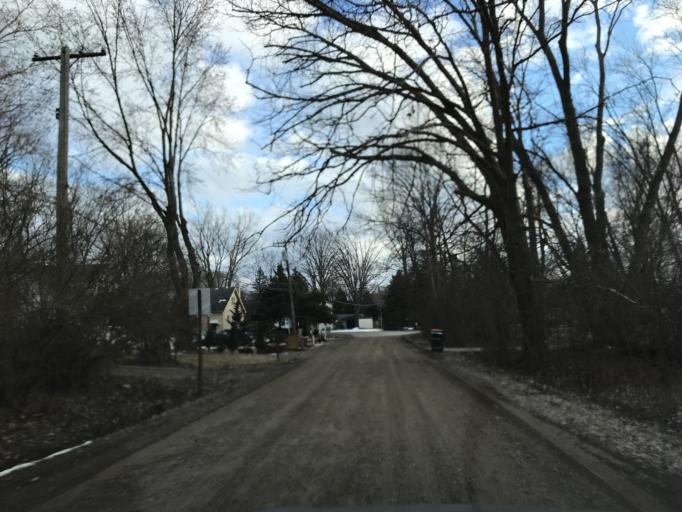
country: US
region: Michigan
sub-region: Oakland County
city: Farmington
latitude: 42.4533
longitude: -83.3272
